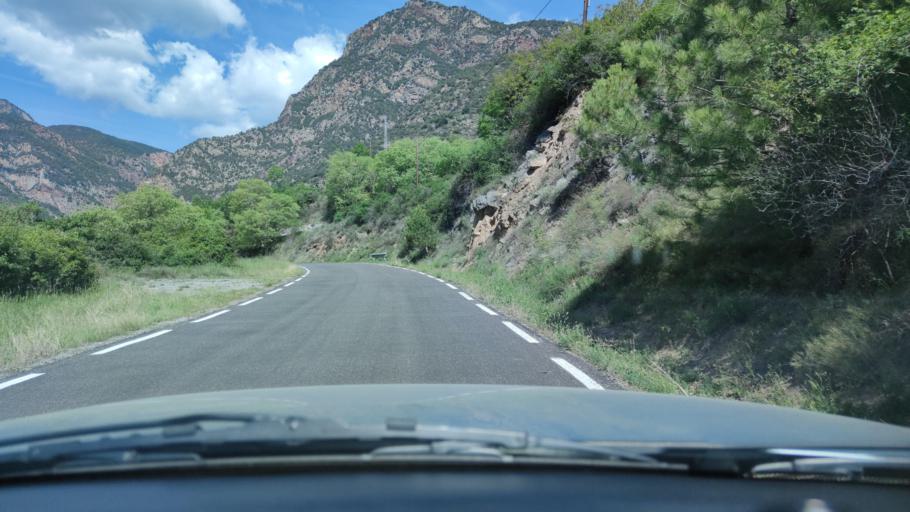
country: ES
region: Catalonia
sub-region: Provincia de Lleida
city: Coll de Nargo
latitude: 42.2942
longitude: 1.3161
